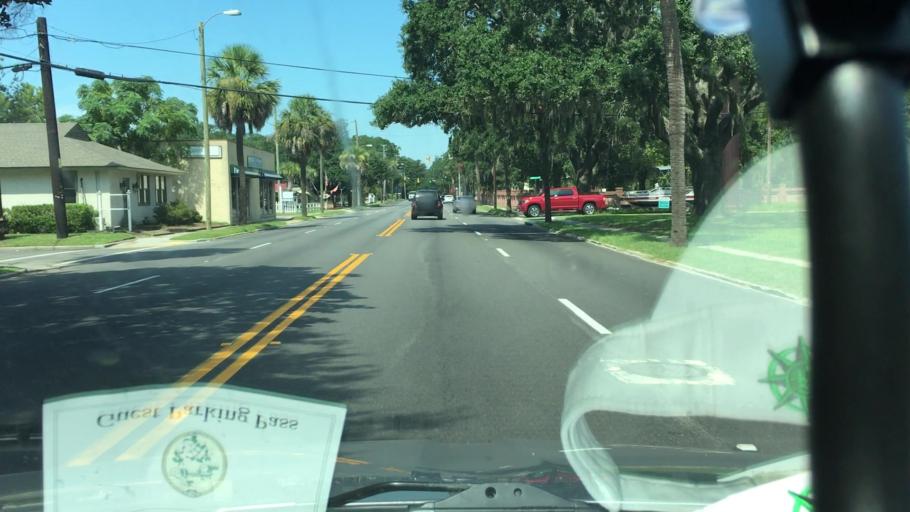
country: US
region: South Carolina
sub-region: Beaufort County
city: Beaufort
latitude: 32.4397
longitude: -80.6771
